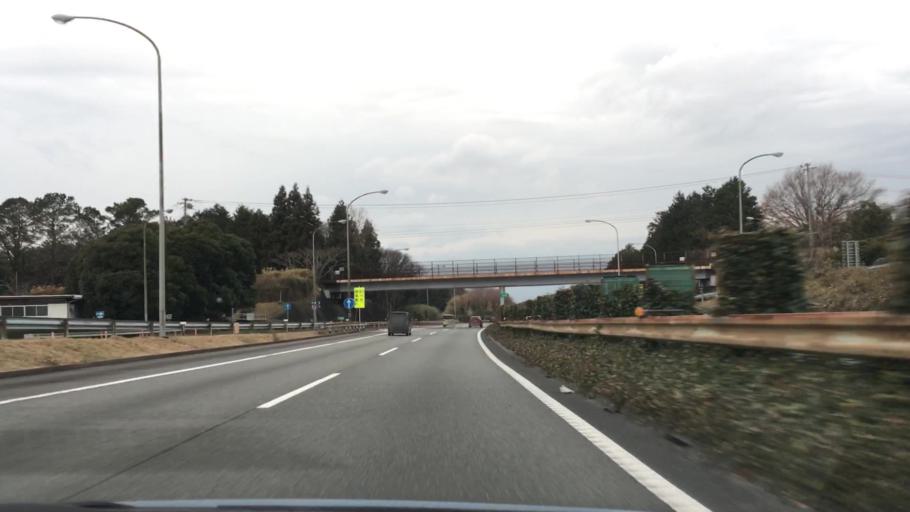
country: JP
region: Shizuoka
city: Numazu
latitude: 35.1429
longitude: 138.8358
